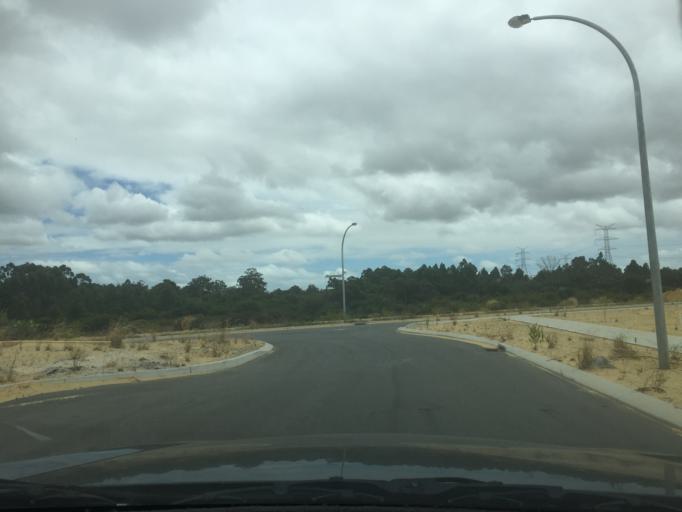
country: AU
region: Western Australia
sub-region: Armadale
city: Harrisdale
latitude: -32.1352
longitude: 115.9066
